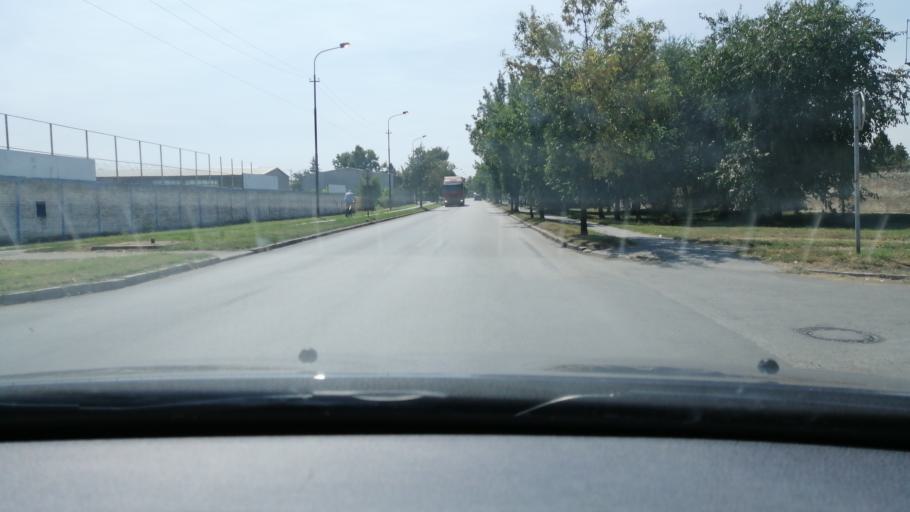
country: RS
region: Autonomna Pokrajina Vojvodina
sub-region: Srednjebanatski Okrug
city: Zrenjanin
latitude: 45.3974
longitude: 20.3928
